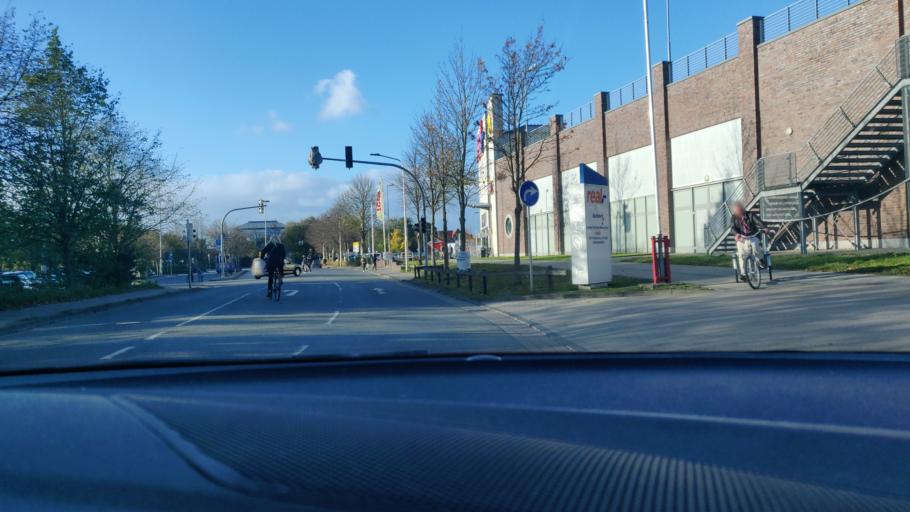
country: DE
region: Lower Saxony
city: Cuxhaven
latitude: 53.8614
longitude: 8.7046
